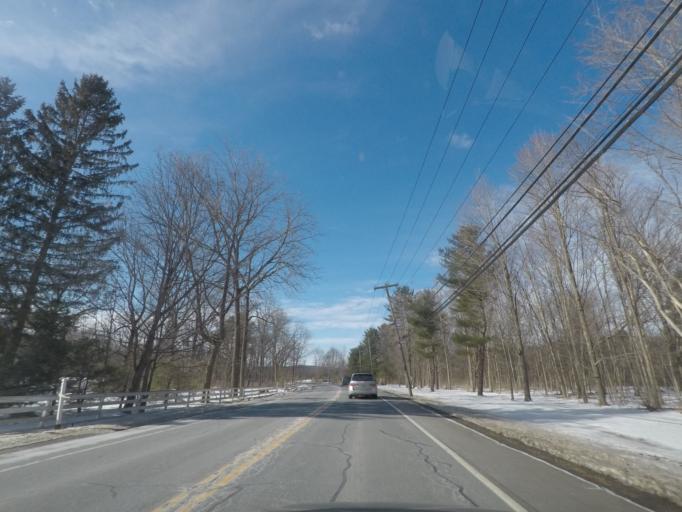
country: US
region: New York
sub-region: Albany County
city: Altamont
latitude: 42.7104
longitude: -73.9850
